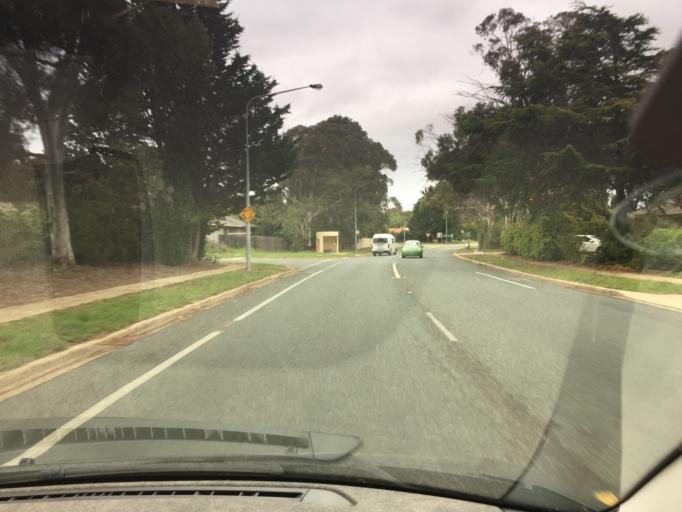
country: AU
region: Australian Capital Territory
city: Kaleen
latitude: -35.2286
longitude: 149.1113
